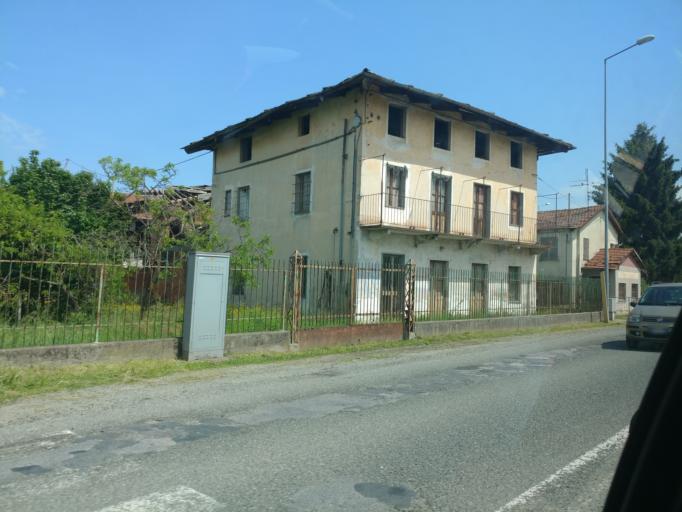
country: IT
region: Piedmont
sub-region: Provincia di Torino
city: Cavour
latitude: 44.7466
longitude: 7.4097
